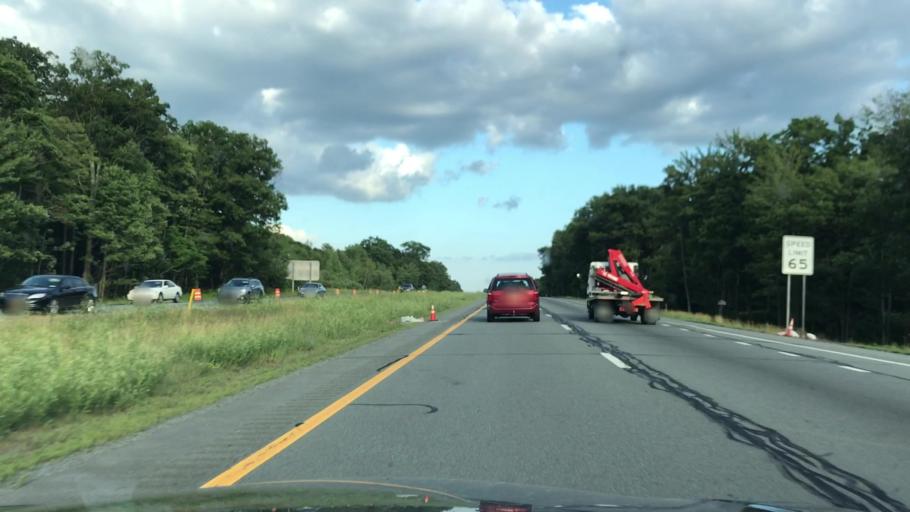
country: US
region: New York
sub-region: Sullivan County
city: Rock Hill
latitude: 41.6049
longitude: -74.5614
